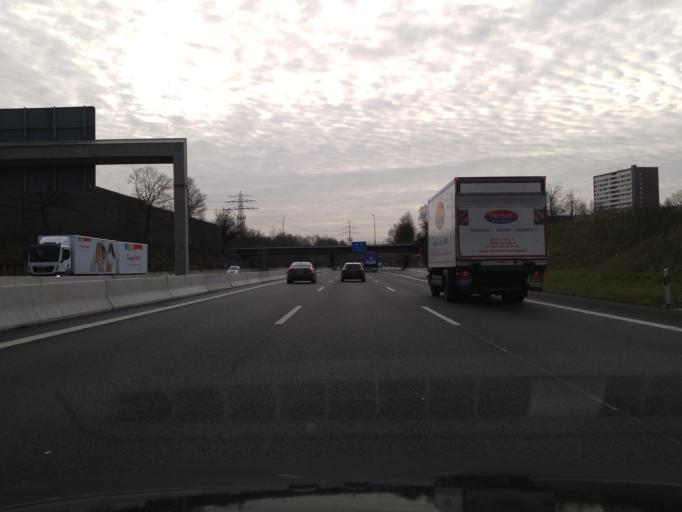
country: DE
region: Schleswig-Holstein
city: Oststeinbek
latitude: 53.5456
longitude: 10.1475
